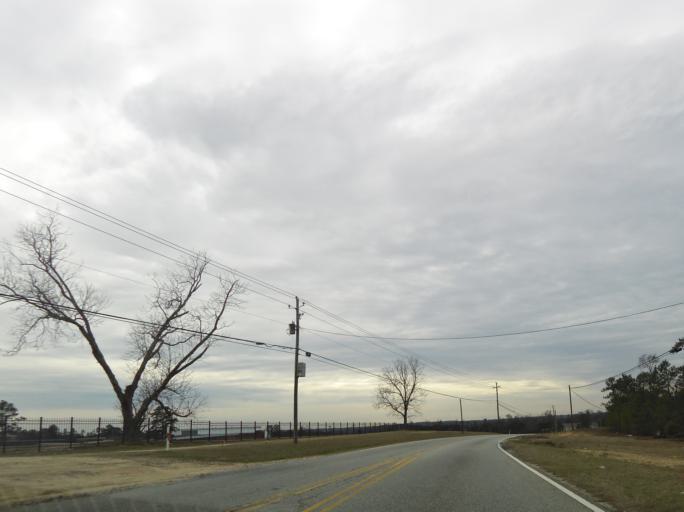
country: US
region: Georgia
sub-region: Bibb County
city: West Point
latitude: 32.8146
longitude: -83.7338
